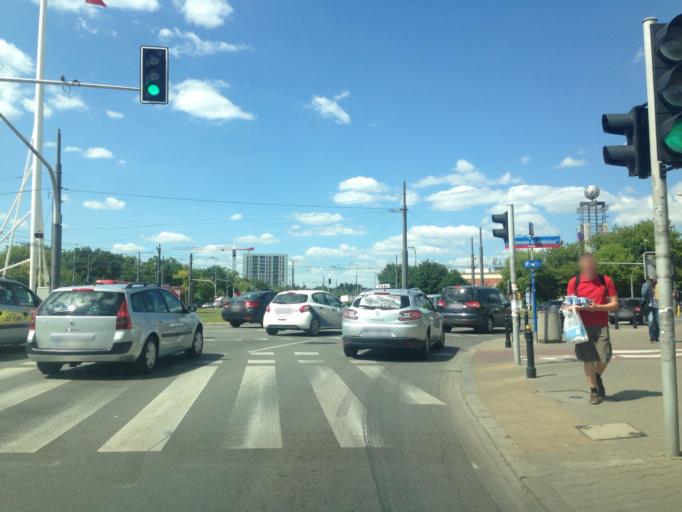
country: PL
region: Masovian Voivodeship
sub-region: Warszawa
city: Wola
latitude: 52.2541
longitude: 20.9833
